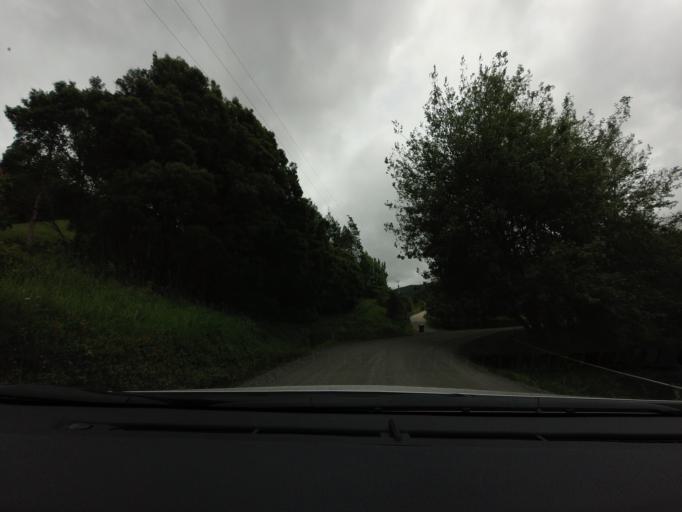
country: NZ
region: Auckland
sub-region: Auckland
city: Warkworth
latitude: -36.4920
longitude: 174.6215
